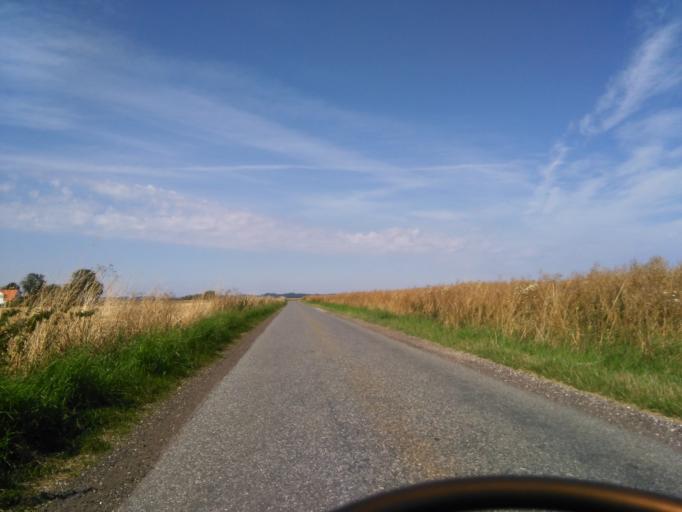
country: DK
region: Central Jutland
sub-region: Hedensted Kommune
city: Juelsminde
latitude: 55.8523
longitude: 10.0475
